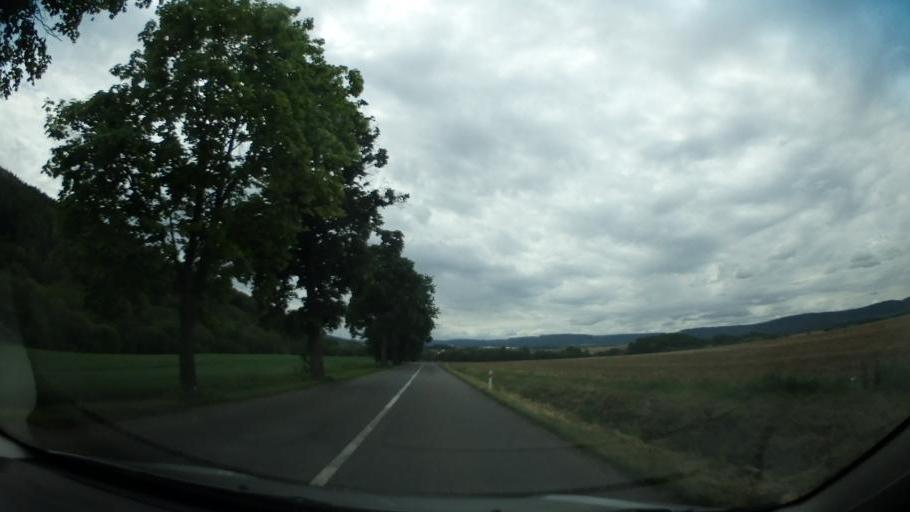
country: CZ
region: Pardubicky
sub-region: Okres Svitavy
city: Moravska Trebova
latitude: 49.7844
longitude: 16.6692
